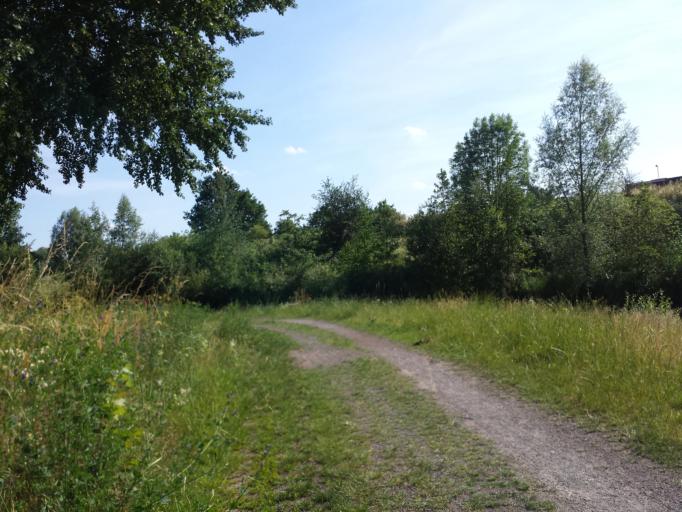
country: DE
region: Lower Saxony
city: Stuhr
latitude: 53.0876
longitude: 8.7495
